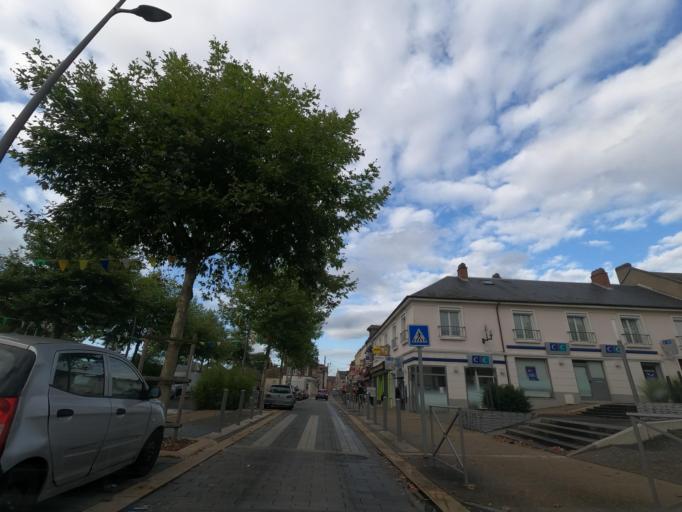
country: FR
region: Haute-Normandie
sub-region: Departement de la Seine-Maritime
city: Grand-Couronne
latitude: 49.3576
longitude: 1.0085
